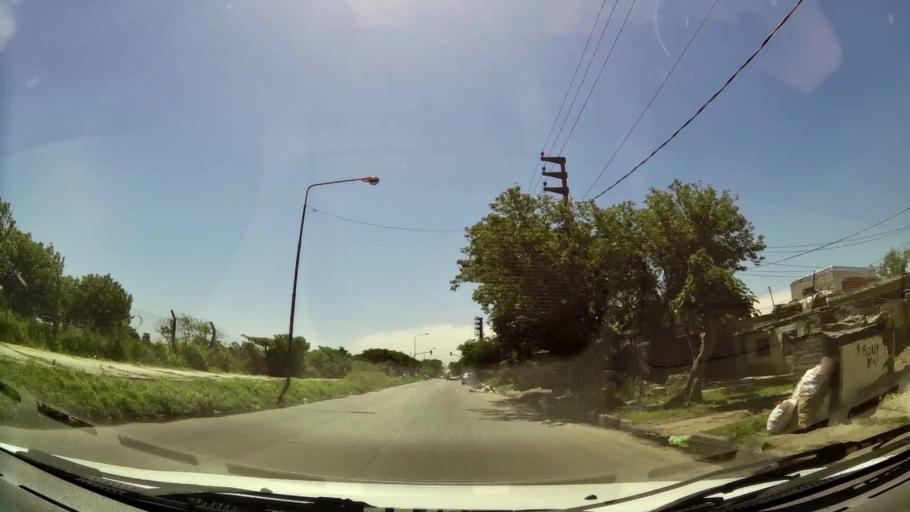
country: AR
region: Buenos Aires
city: Caseros
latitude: -34.5664
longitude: -58.5776
